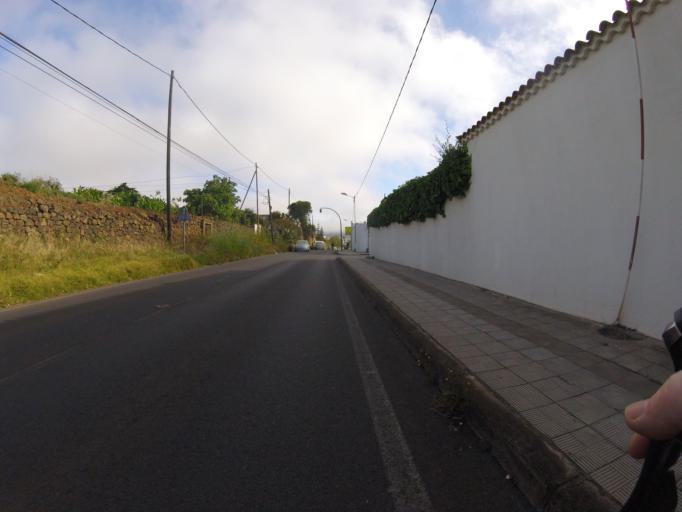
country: ES
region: Canary Islands
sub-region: Provincia de Santa Cruz de Tenerife
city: La Laguna
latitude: 28.4770
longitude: -16.3182
